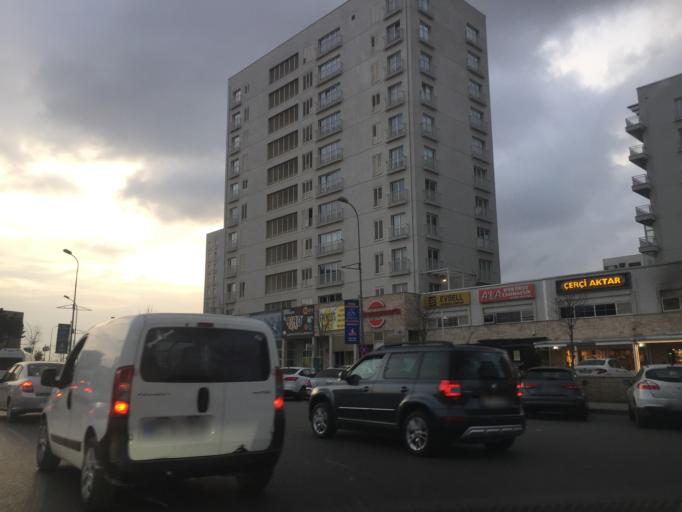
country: TR
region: Istanbul
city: Samandira
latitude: 40.9907
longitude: 29.2285
